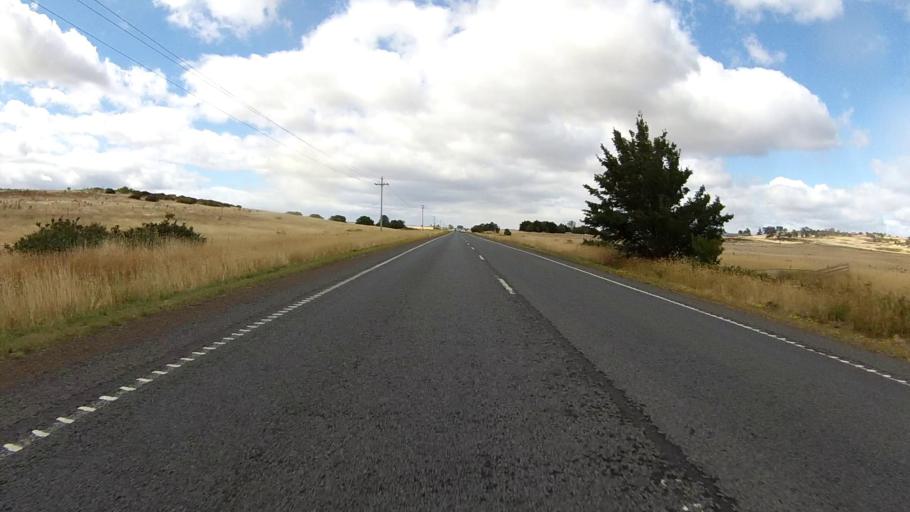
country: AU
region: Tasmania
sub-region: Northern Midlands
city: Evandale
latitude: -41.8490
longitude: 147.4504
